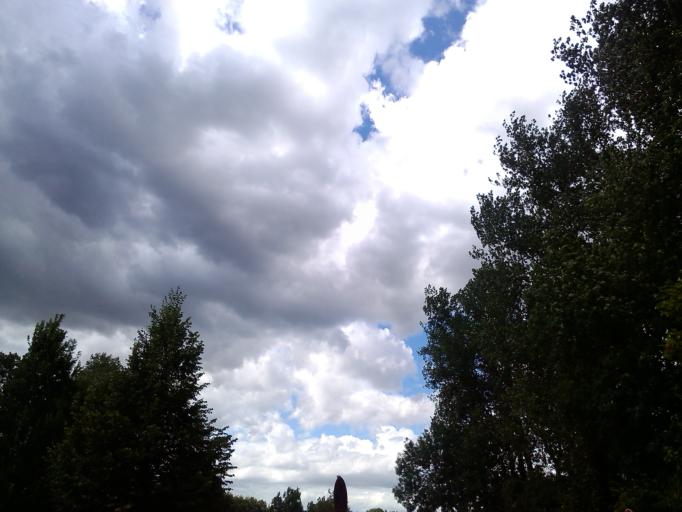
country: DE
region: Bavaria
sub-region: Upper Bavaria
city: Grobenzell
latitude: 48.1977
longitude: 11.4146
